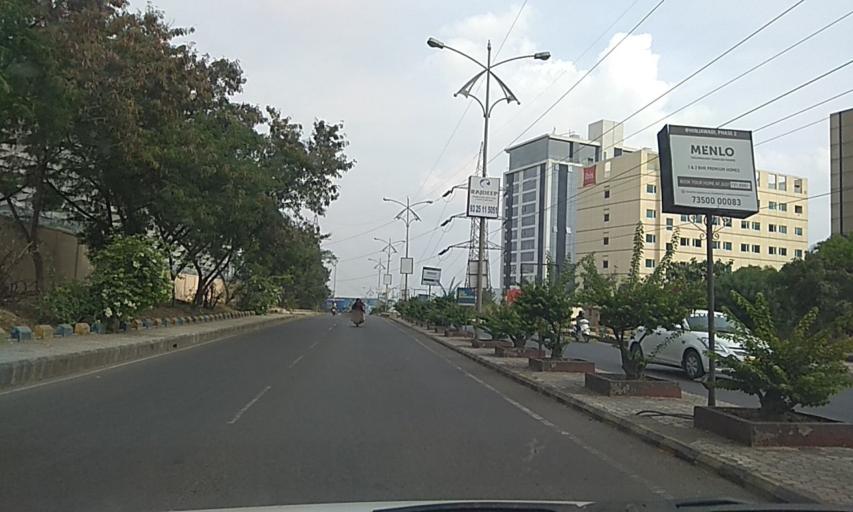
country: IN
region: Maharashtra
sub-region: Pune Division
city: Pimpri
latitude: 18.5964
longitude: 73.7159
